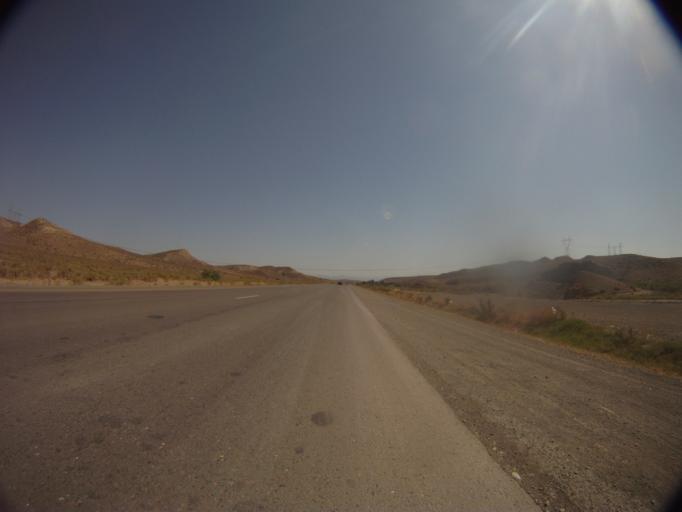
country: AZ
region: Agstafa
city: Saloglu
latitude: 41.2212
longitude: 45.2899
